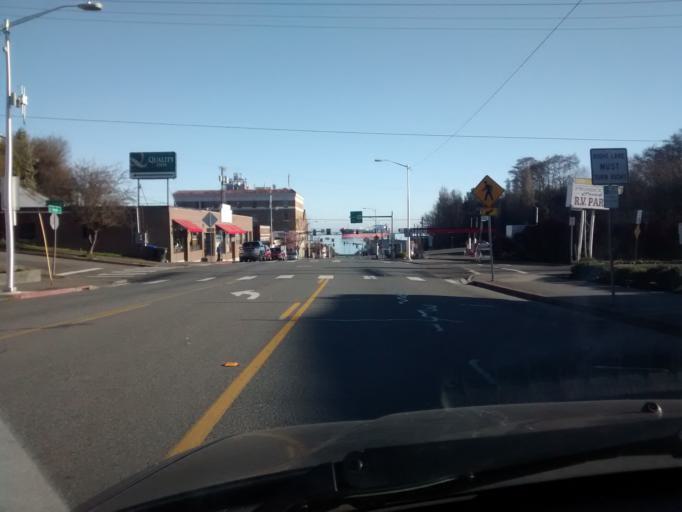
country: US
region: Washington
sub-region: Clallam County
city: Port Angeles
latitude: 48.1171
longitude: -123.4328
